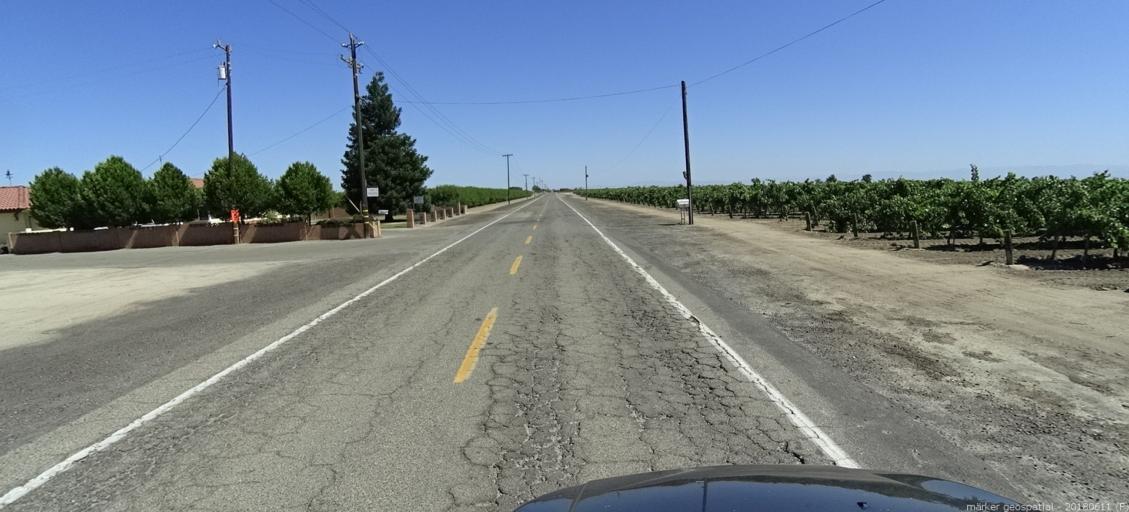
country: US
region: California
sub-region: Madera County
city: Fairmead
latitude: 36.9715
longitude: -120.2023
